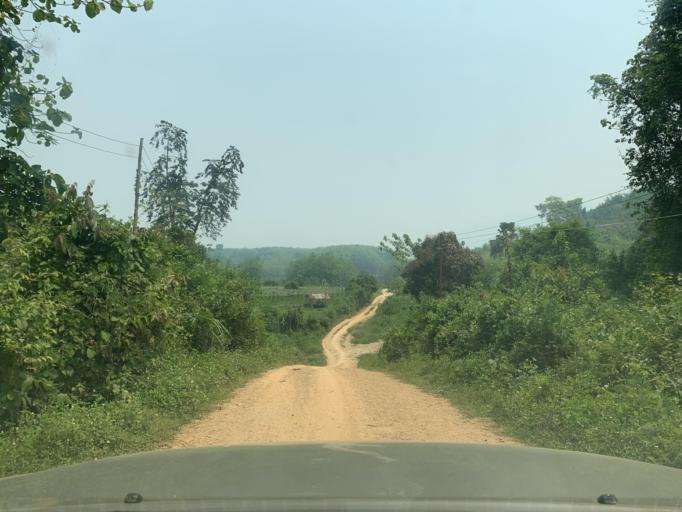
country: LA
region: Louangphabang
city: Xiang Ngeun
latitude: 19.8232
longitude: 102.2112
